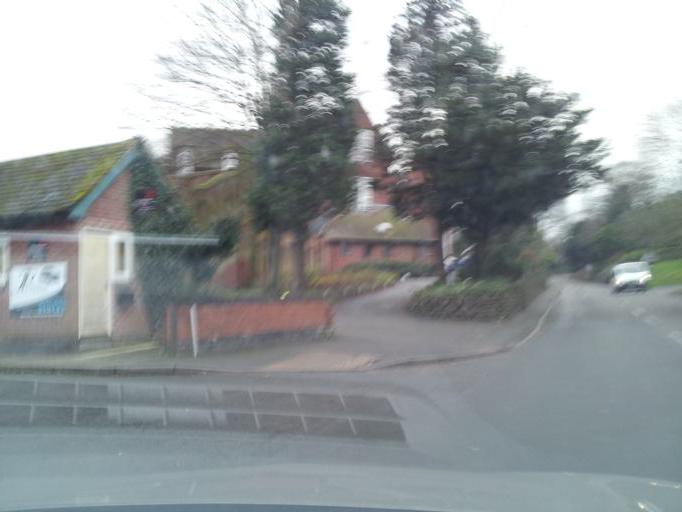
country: GB
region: England
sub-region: Derbyshire
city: Repton
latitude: 52.8391
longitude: -1.5514
